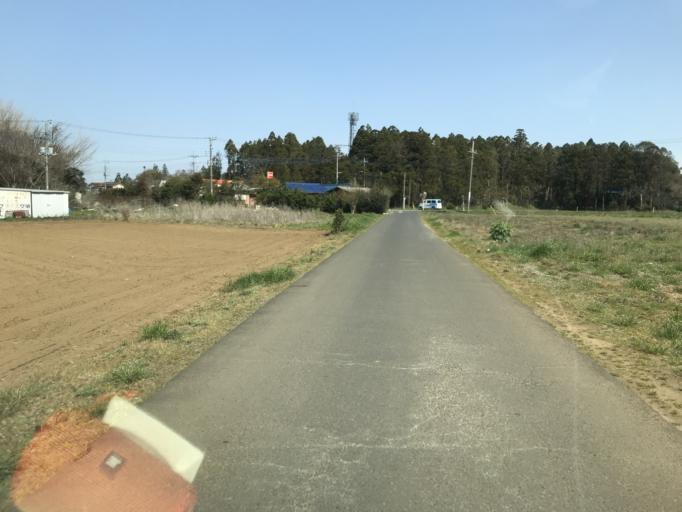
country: JP
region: Chiba
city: Sawara
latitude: 35.8418
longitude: 140.5248
